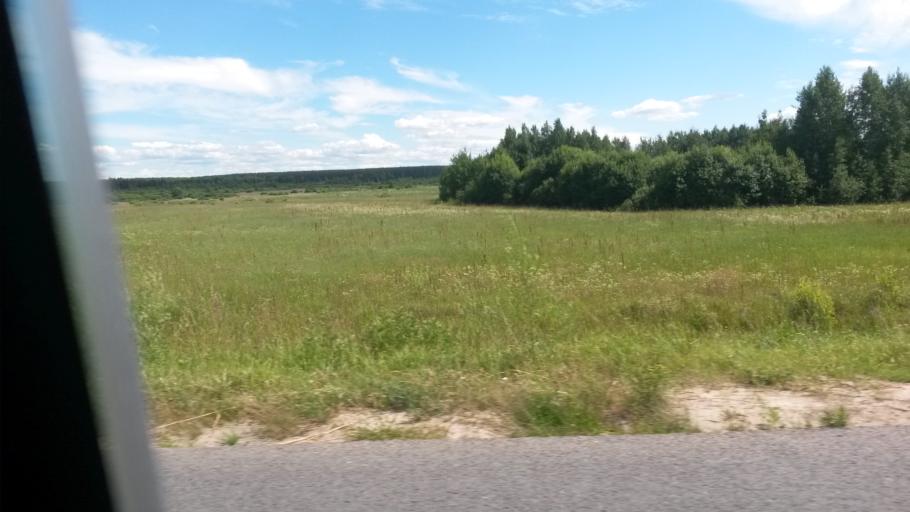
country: RU
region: Ivanovo
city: Staraya Vichuga
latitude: 57.2425
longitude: 41.8910
